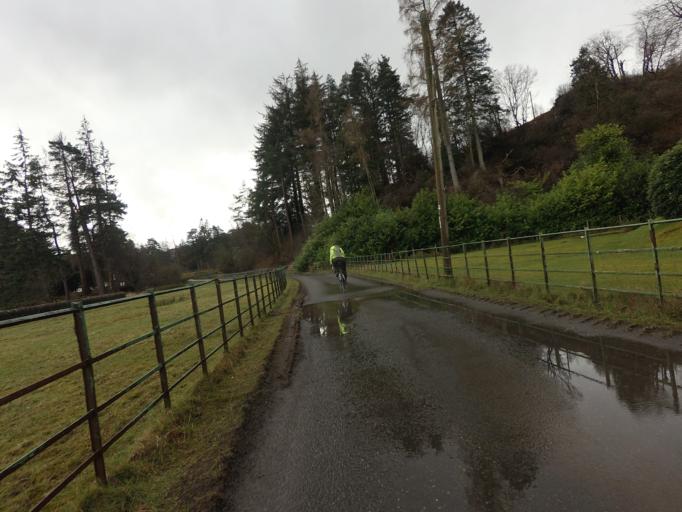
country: GB
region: Scotland
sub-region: West Dunbartonshire
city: Balloch
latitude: 56.2602
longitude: -4.5804
